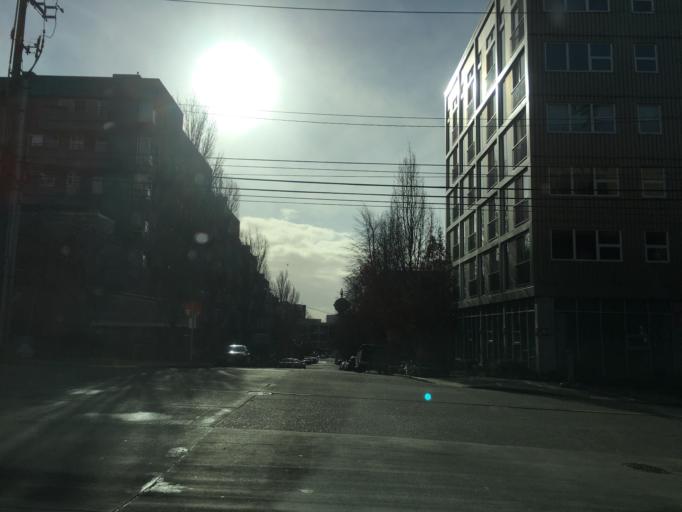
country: US
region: Washington
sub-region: King County
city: Seattle
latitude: 47.6223
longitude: -122.3594
